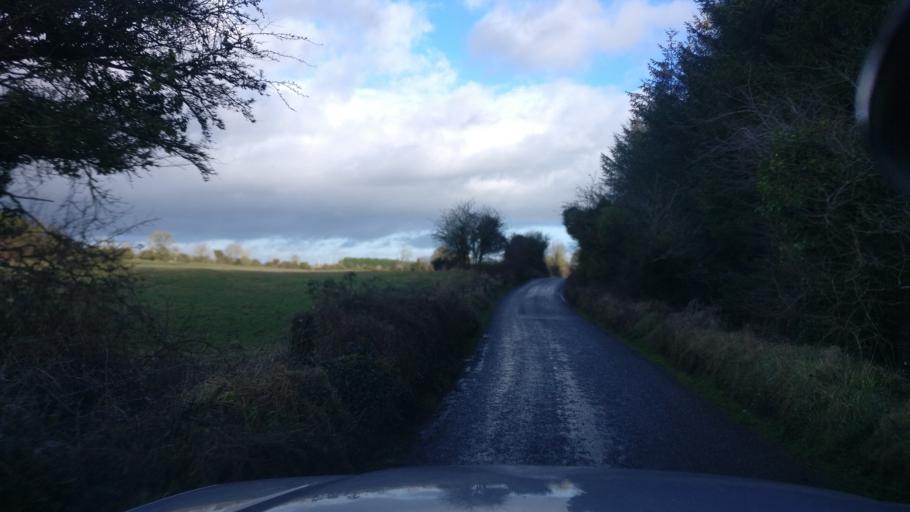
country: IE
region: Connaught
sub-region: County Galway
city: Loughrea
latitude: 53.2570
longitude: -8.6218
